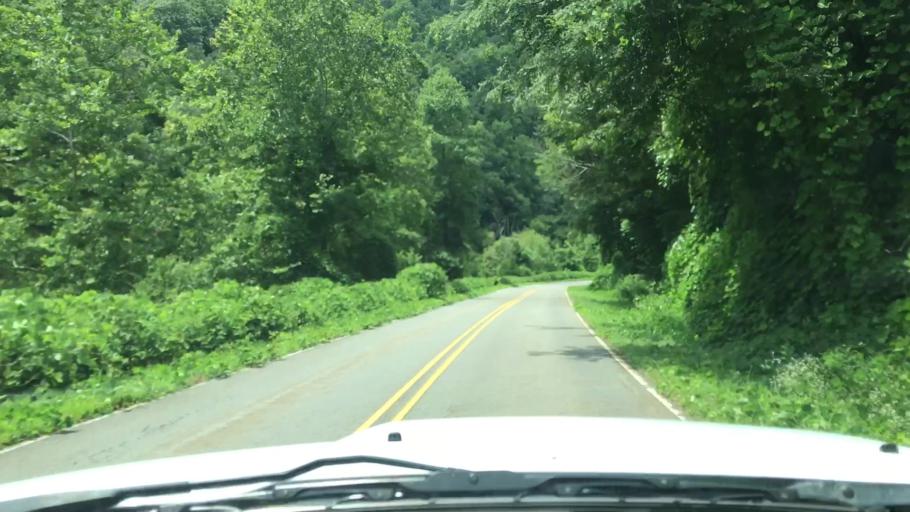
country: US
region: North Carolina
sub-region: Graham County
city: Robbinsville
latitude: 35.4402
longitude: -83.9338
